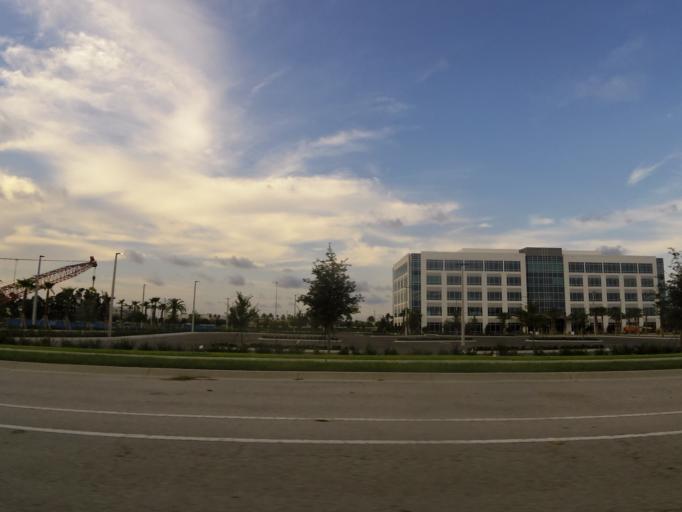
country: US
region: Florida
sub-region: Saint Johns County
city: Ponte Vedra Beach
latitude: 30.2482
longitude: -81.5246
